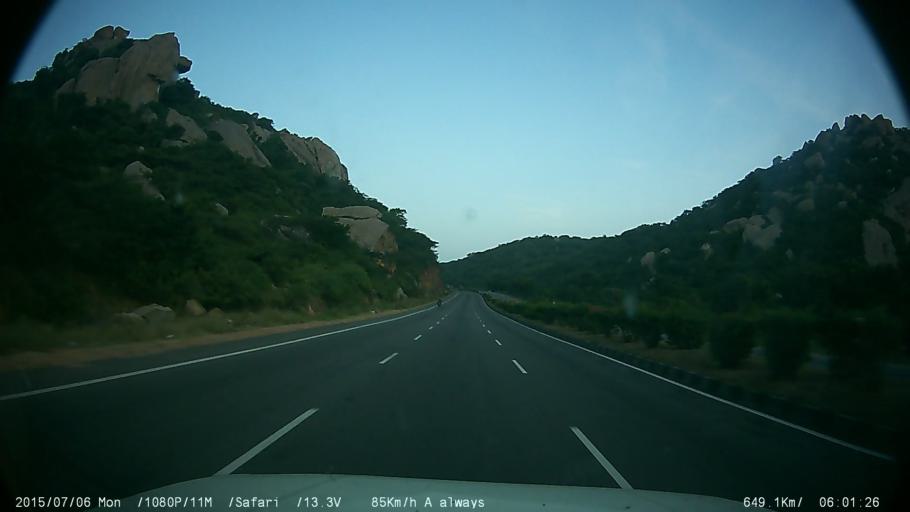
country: IN
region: Tamil Nadu
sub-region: Krishnagiri
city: Krishnagiri
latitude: 12.6054
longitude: 78.1177
